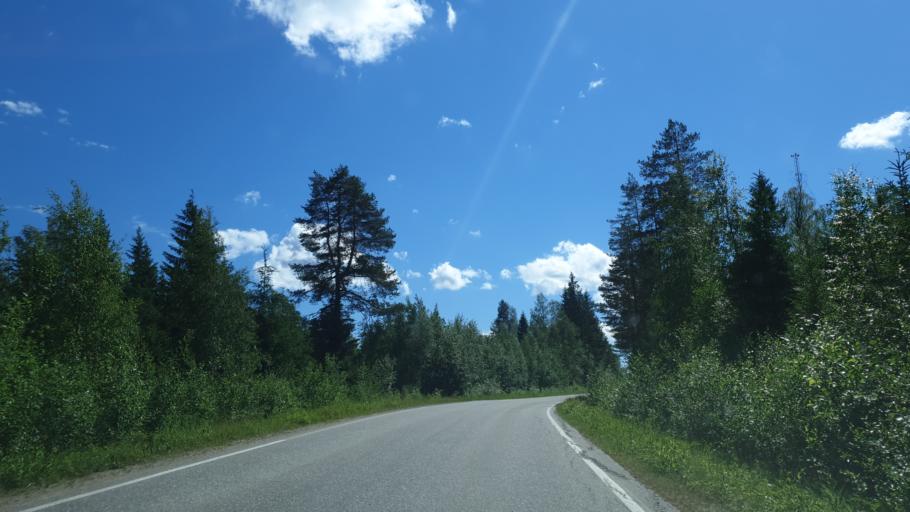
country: FI
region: Northern Savo
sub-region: Koillis-Savo
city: Kaavi
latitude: 62.9948
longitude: 28.5046
